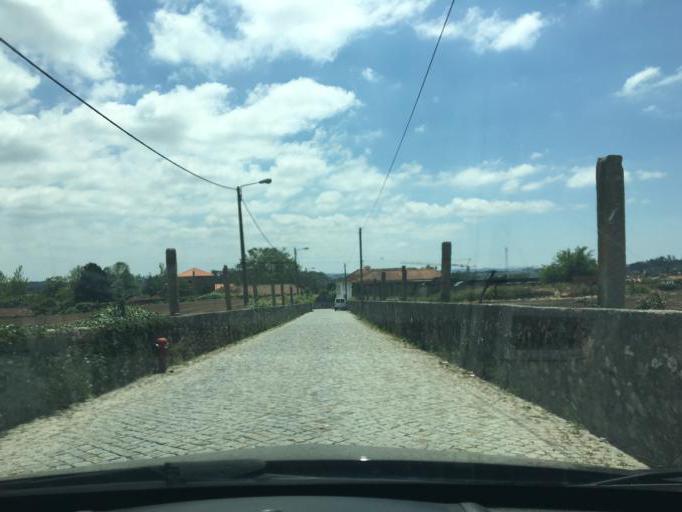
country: PT
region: Porto
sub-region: Maia
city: Anta
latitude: 41.2866
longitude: -8.6155
